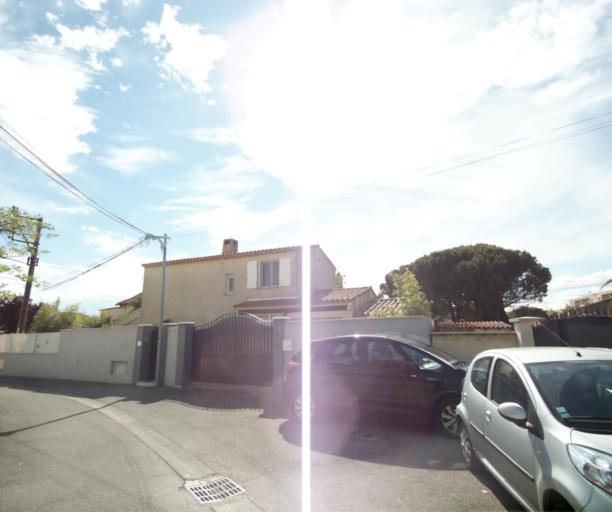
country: FR
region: Provence-Alpes-Cote d'Azur
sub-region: Departement des Bouches-du-Rhone
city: Rognac
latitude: 43.4885
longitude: 5.2268
